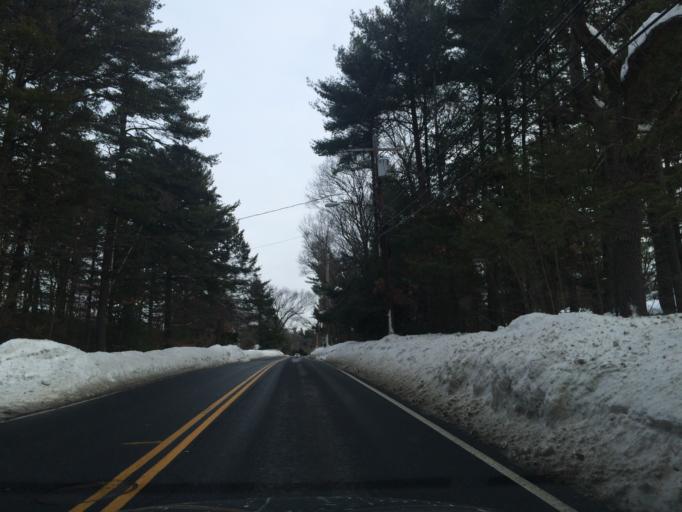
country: US
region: Massachusetts
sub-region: Middlesex County
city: Weston
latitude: 42.3560
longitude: -71.3010
